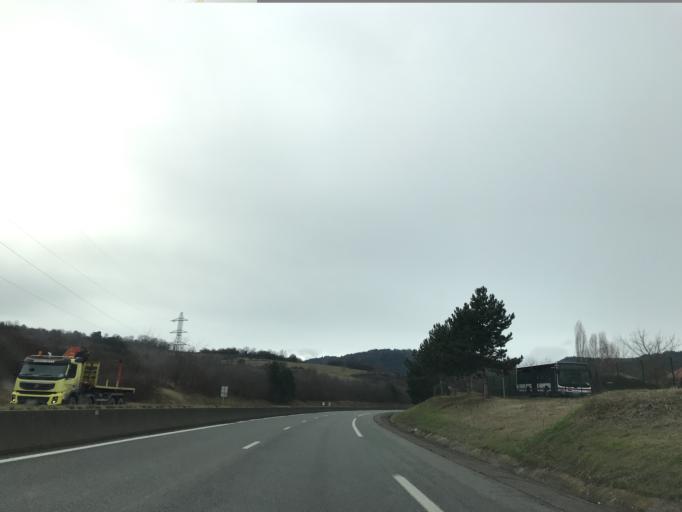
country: FR
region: Auvergne
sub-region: Departement du Puy-de-Dome
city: Beaumont
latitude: 45.7438
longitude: 3.0870
